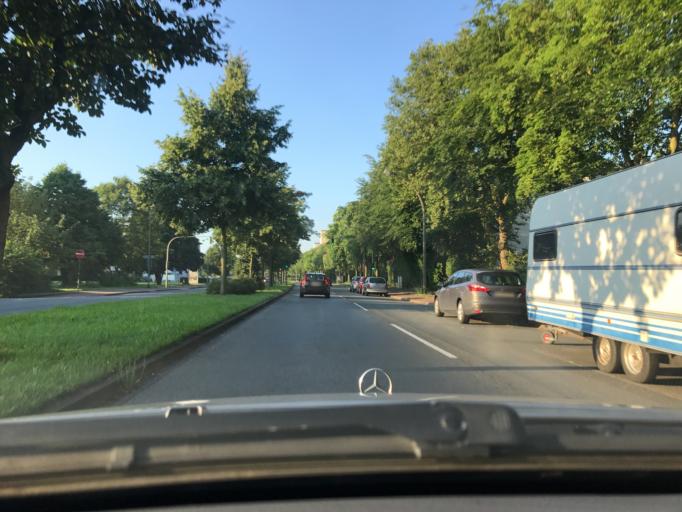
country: DE
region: North Rhine-Westphalia
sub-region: Regierungsbezirk Dusseldorf
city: Hochfeld
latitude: 51.4016
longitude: 6.7104
